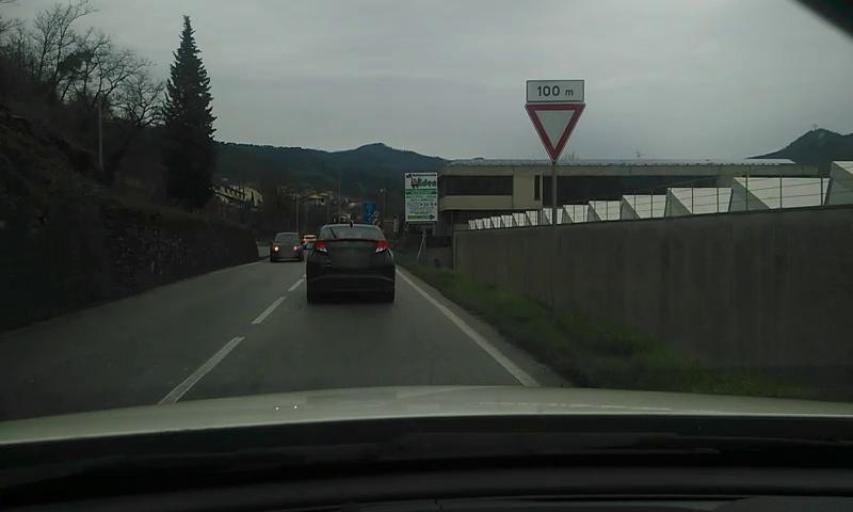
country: IT
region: Tuscany
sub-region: Provincia di Prato
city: Vaiano
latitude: 43.9541
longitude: 11.1267
